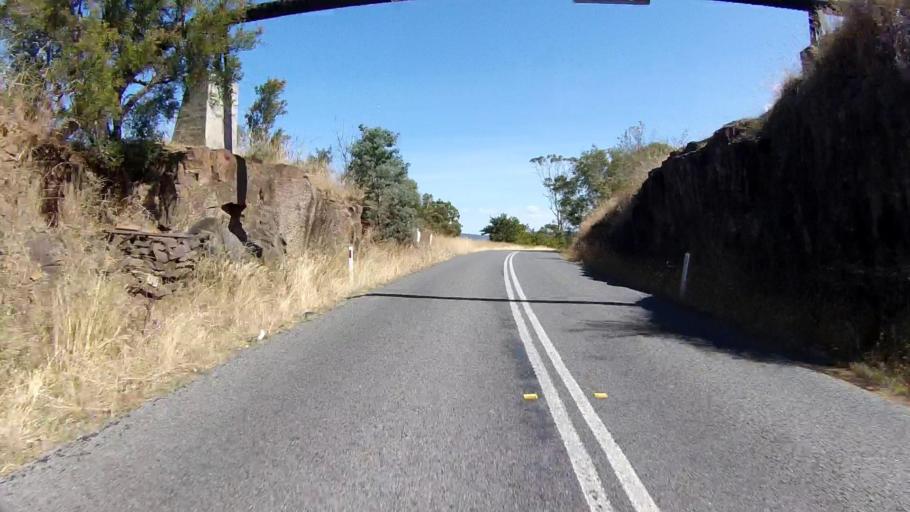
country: AU
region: Tasmania
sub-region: Sorell
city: Sorell
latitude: -42.4910
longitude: 147.9329
